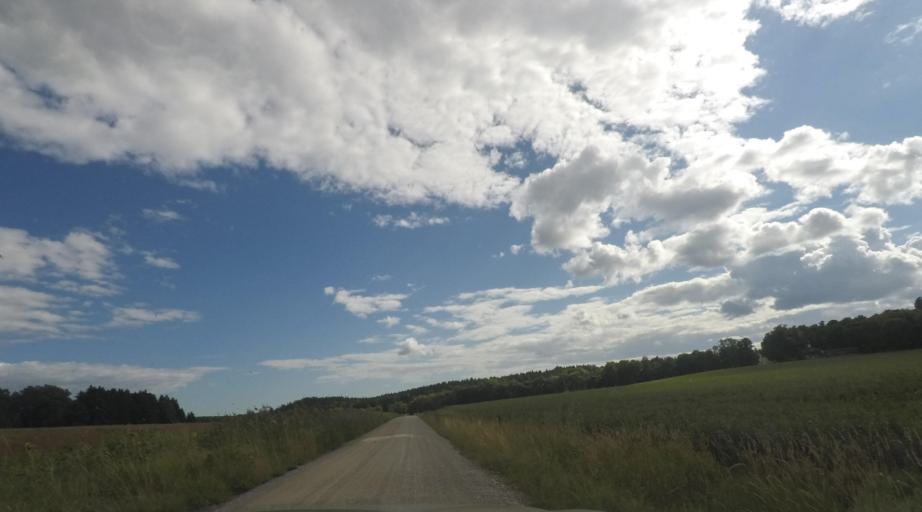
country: SE
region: Stockholm
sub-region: Sodertalje Kommun
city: Pershagen
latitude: 59.1134
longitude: 17.6671
